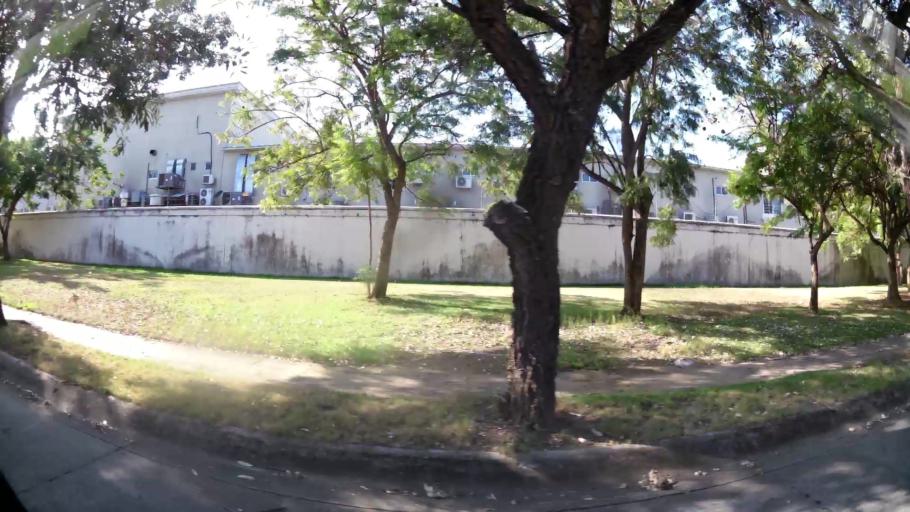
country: EC
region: Guayas
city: Santa Lucia
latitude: -2.1839
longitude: -79.9859
